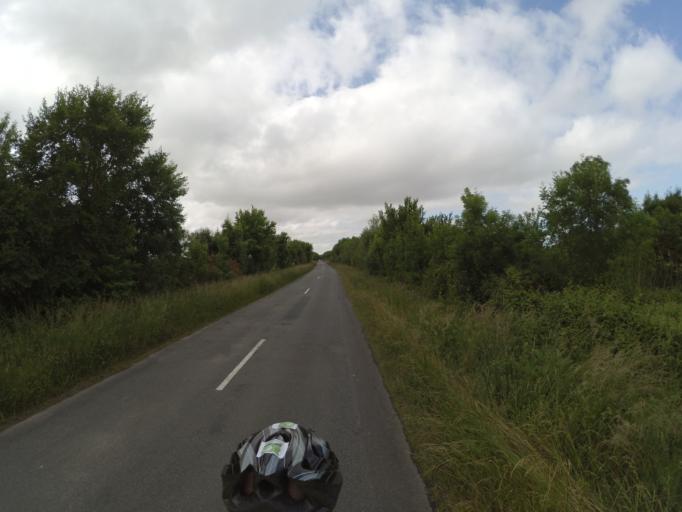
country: FR
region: Poitou-Charentes
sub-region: Departement de la Charente-Maritime
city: Yves
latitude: 46.0413
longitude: -1.0409
